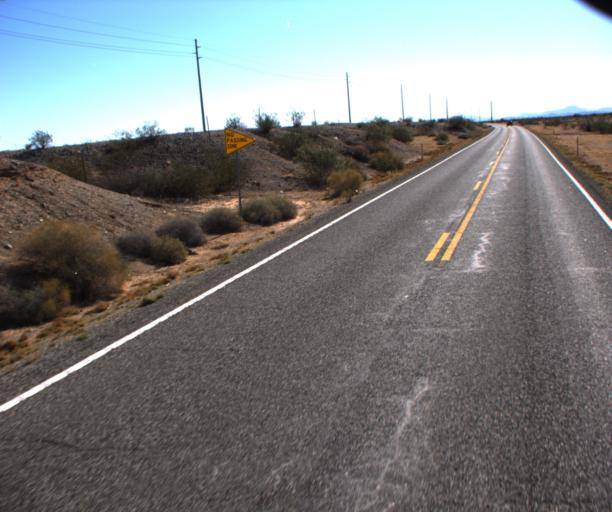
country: US
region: Arizona
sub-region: La Paz County
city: Parker
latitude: 33.9947
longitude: -114.1718
